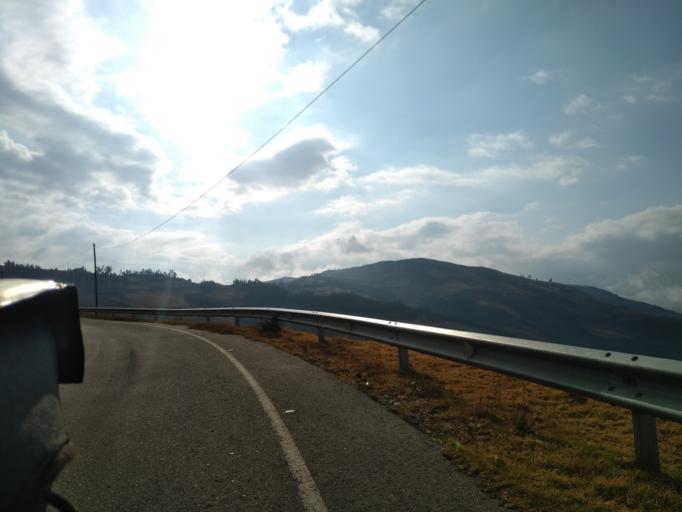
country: PE
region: La Libertad
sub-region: Provincia de Otuzco
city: Agallpampa
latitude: -7.9830
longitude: -78.5360
